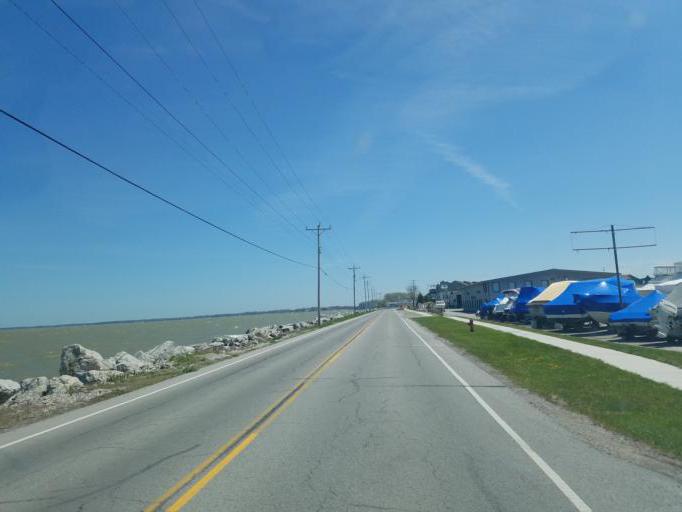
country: US
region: Ohio
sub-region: Ottawa County
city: Port Clinton
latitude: 41.5196
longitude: -82.9536
